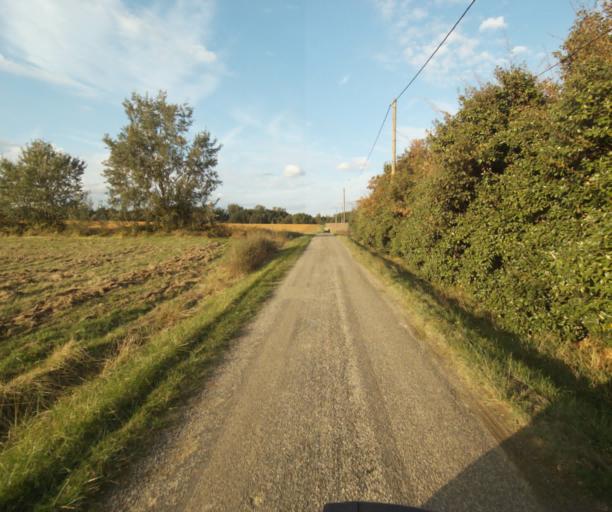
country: FR
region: Midi-Pyrenees
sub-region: Departement de la Haute-Garonne
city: Launac
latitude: 43.8302
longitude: 1.1289
